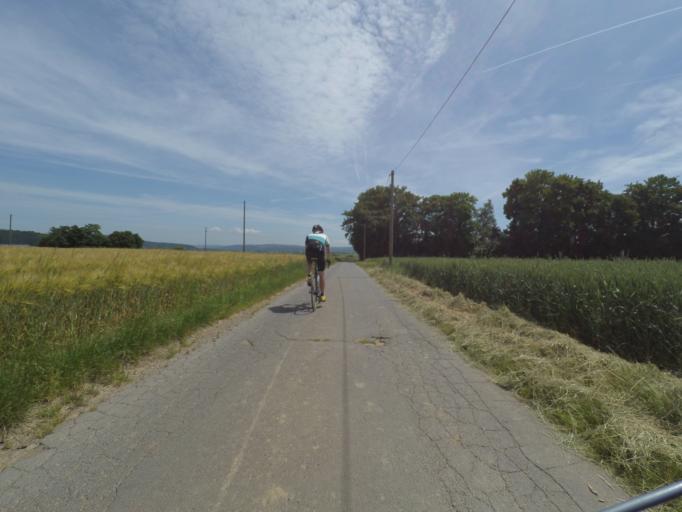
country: DE
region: Rheinland-Pfalz
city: Kobern-Gondorf
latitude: 50.3090
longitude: 7.4408
